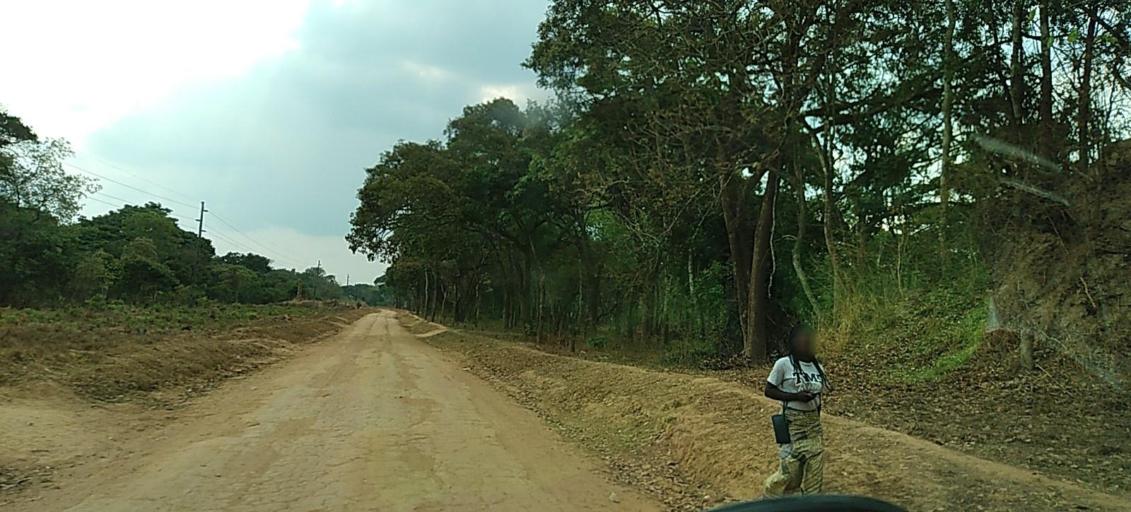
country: ZM
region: North-Western
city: Solwezi
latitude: -12.7848
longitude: 26.5090
